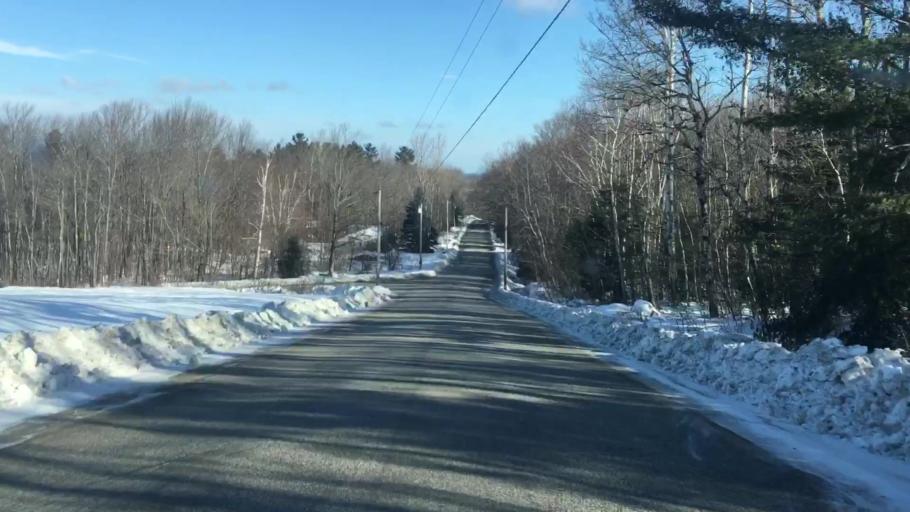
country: US
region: Maine
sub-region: Oxford County
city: Paris
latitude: 44.2783
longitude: -70.4350
